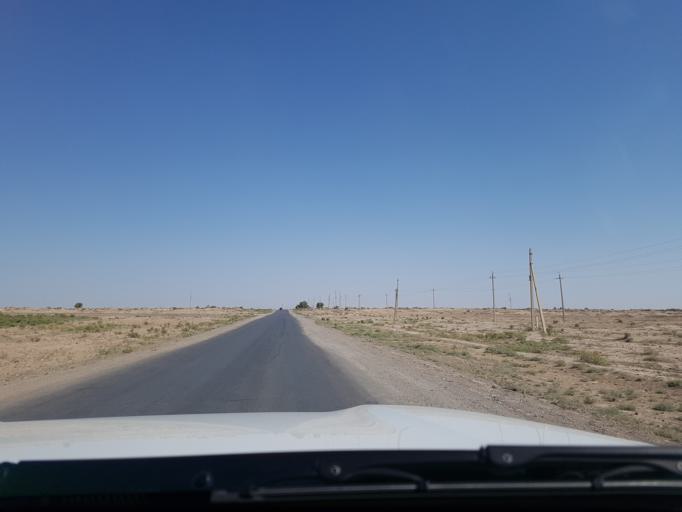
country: IR
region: Razavi Khorasan
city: Sarakhs
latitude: 36.5233
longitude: 61.2396
